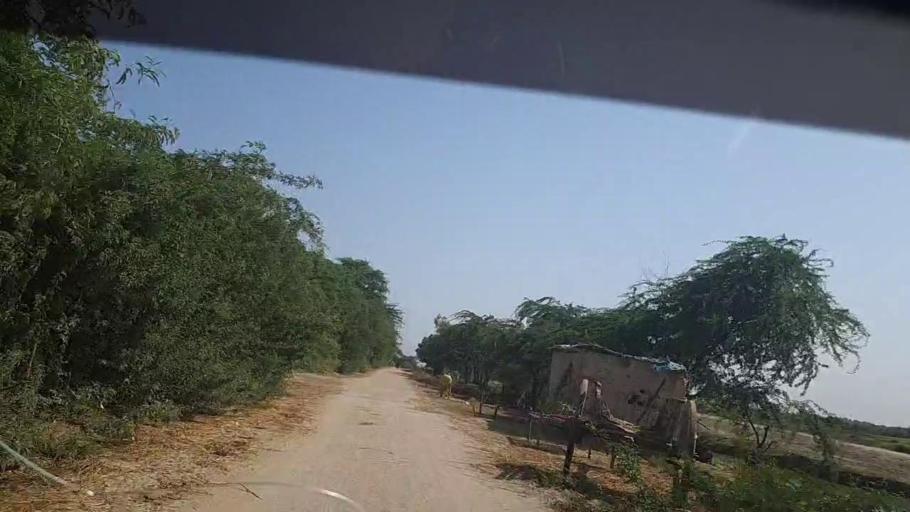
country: PK
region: Sindh
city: Rajo Khanani
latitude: 24.9788
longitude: 68.8663
